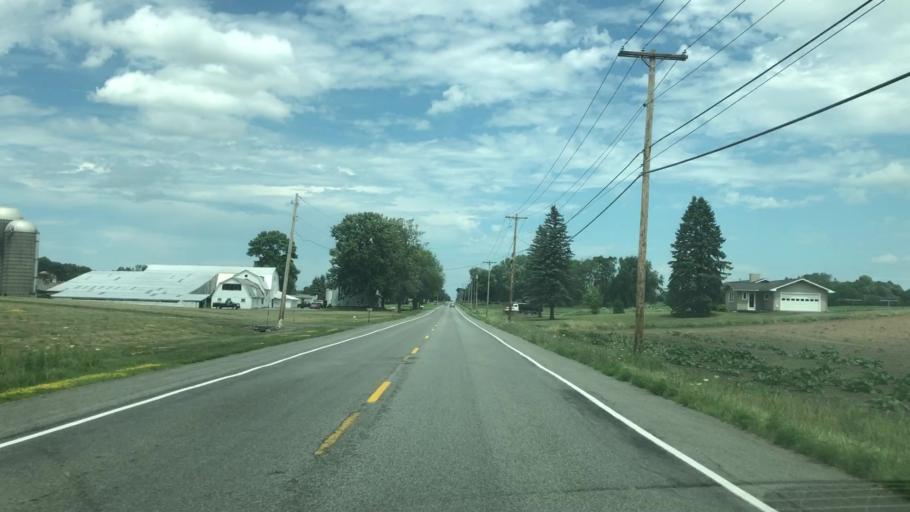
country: US
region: New York
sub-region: Monroe County
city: Fairport
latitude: 43.1461
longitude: -77.4006
